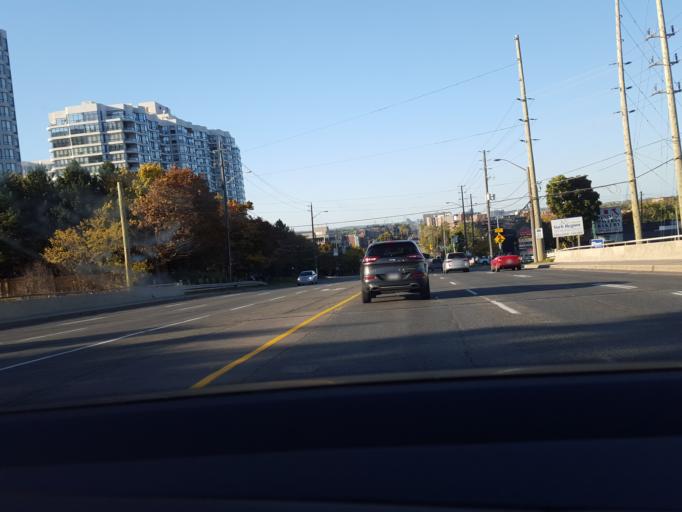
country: CA
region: Ontario
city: North York
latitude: 43.8040
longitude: -79.4216
